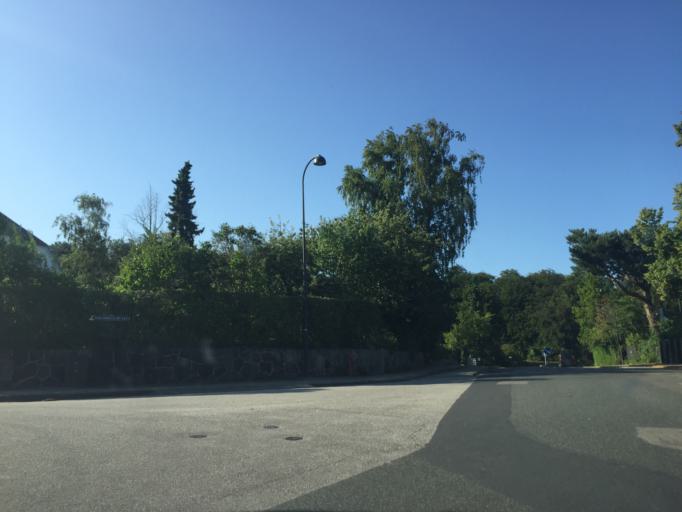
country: DK
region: Capital Region
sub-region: Lyngby-Tarbaek Kommune
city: Kongens Lyngby
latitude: 55.7660
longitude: 12.5358
